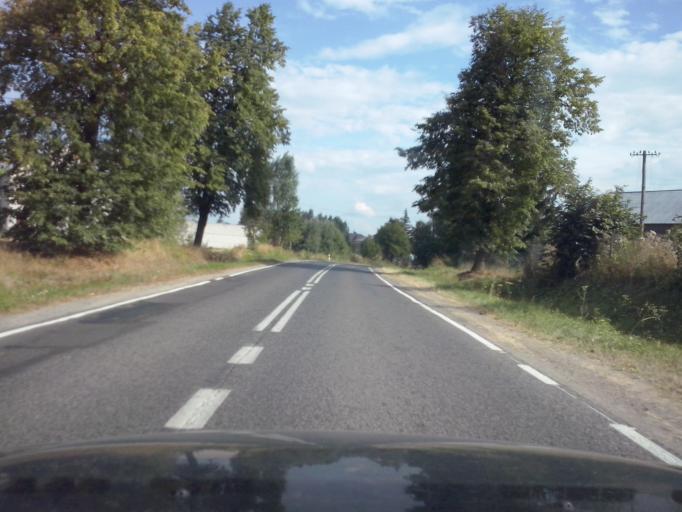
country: PL
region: Swietokrzyskie
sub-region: Powiat kielecki
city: Lagow
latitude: 50.7394
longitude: 21.0719
